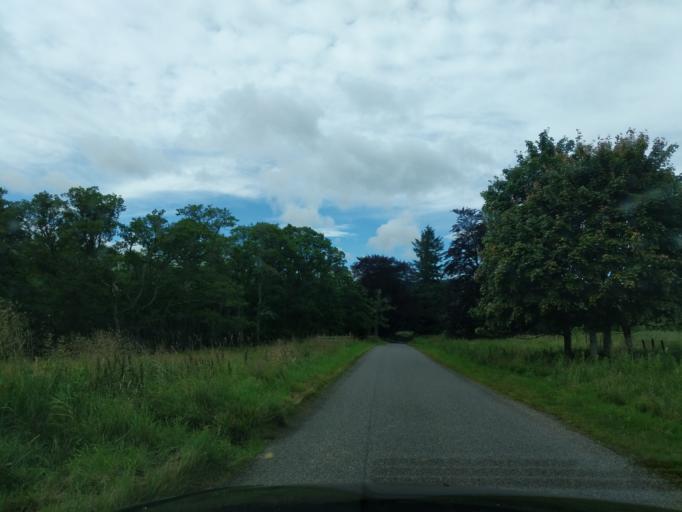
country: GB
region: Scotland
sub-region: Aberdeenshire
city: Aboyne
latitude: 57.0591
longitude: -2.8470
